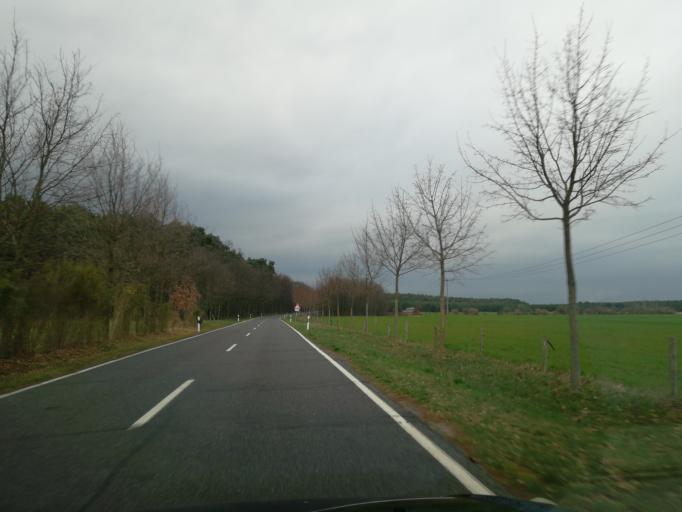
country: DE
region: Brandenburg
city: Vetschau
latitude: 51.7192
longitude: 14.0917
